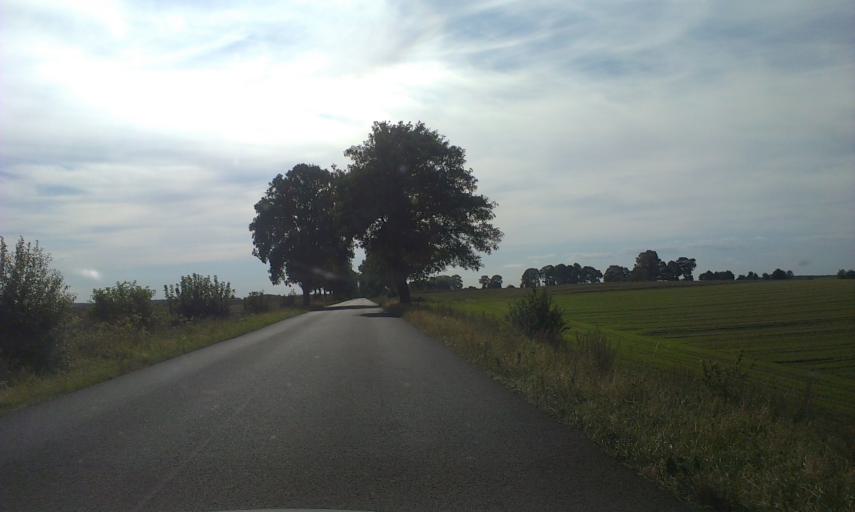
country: PL
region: Greater Poland Voivodeship
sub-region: Powiat zlotowski
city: Zlotow
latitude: 53.4610
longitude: 16.9875
